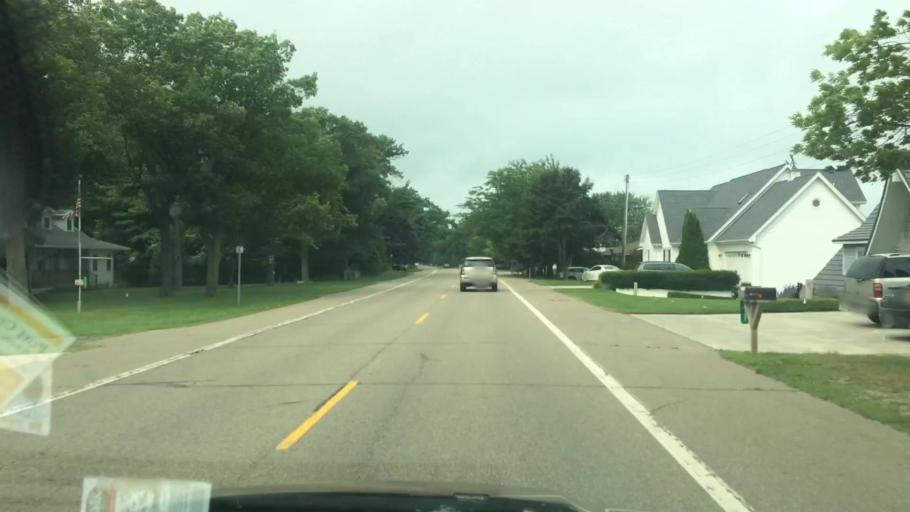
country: US
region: Michigan
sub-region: Huron County
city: Pigeon
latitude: 43.9803
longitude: -83.2208
